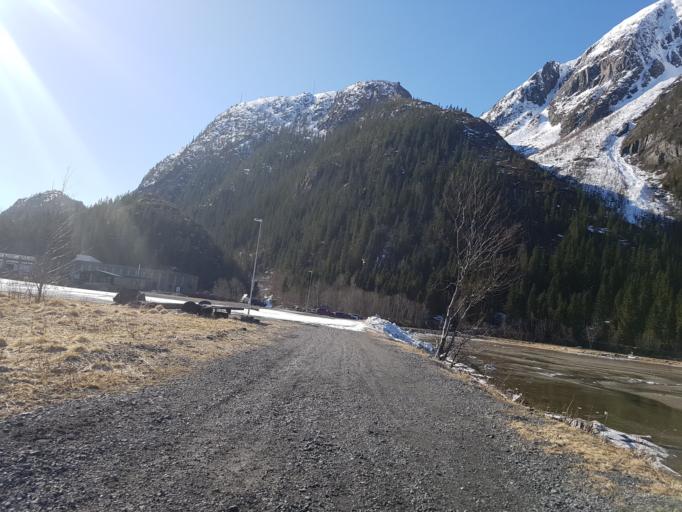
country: NO
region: Nordland
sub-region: Vefsn
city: Mosjoen
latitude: 65.8311
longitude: 13.1925
